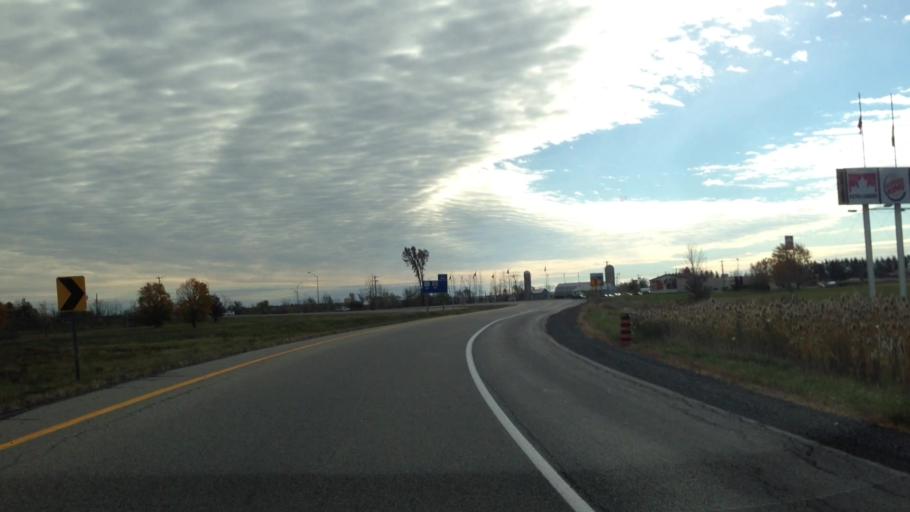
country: CA
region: Ontario
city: Casselman
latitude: 45.3022
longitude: -75.0831
